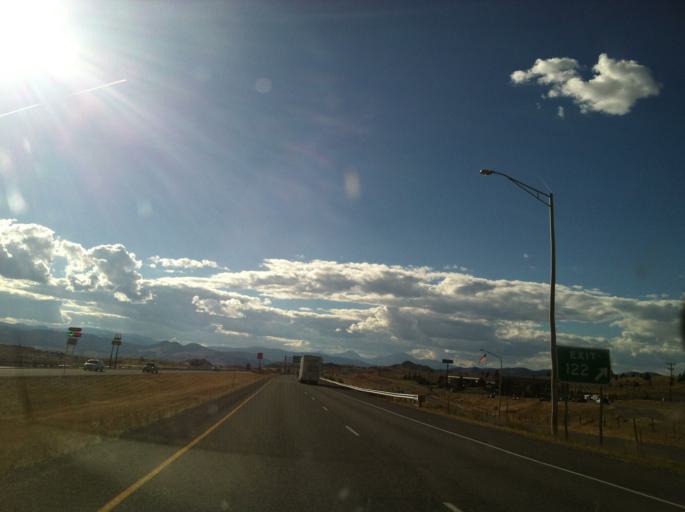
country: US
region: Montana
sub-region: Silver Bow County
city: Butte
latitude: 46.0066
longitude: -112.6074
